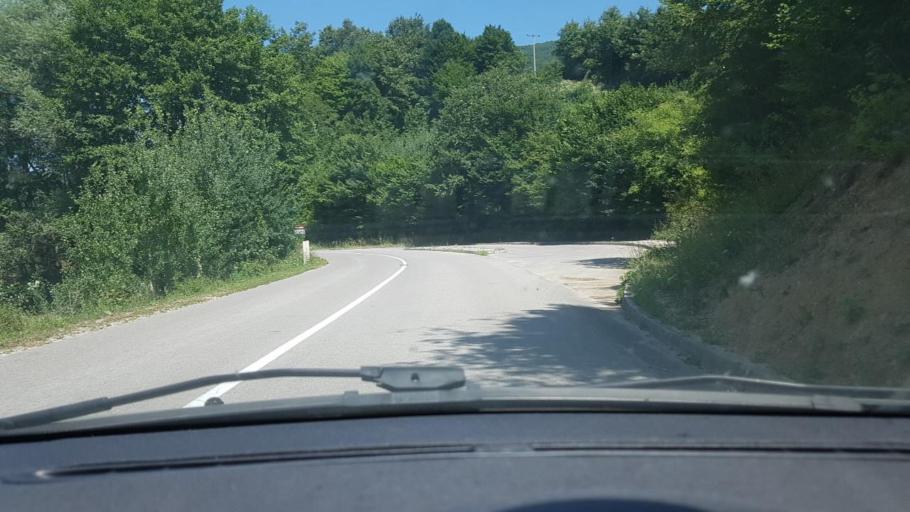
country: BA
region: Federation of Bosnia and Herzegovina
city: Orasac
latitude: 44.5599
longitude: 16.1028
